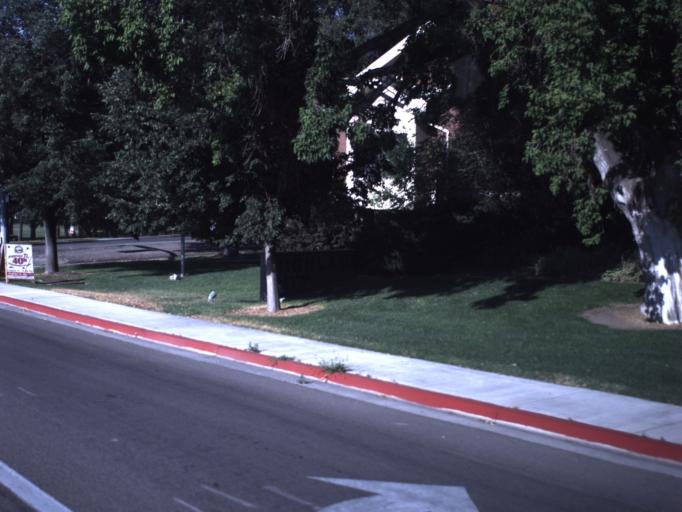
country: US
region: Utah
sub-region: Utah County
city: Cedar Hills
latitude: 40.4213
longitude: -111.7867
